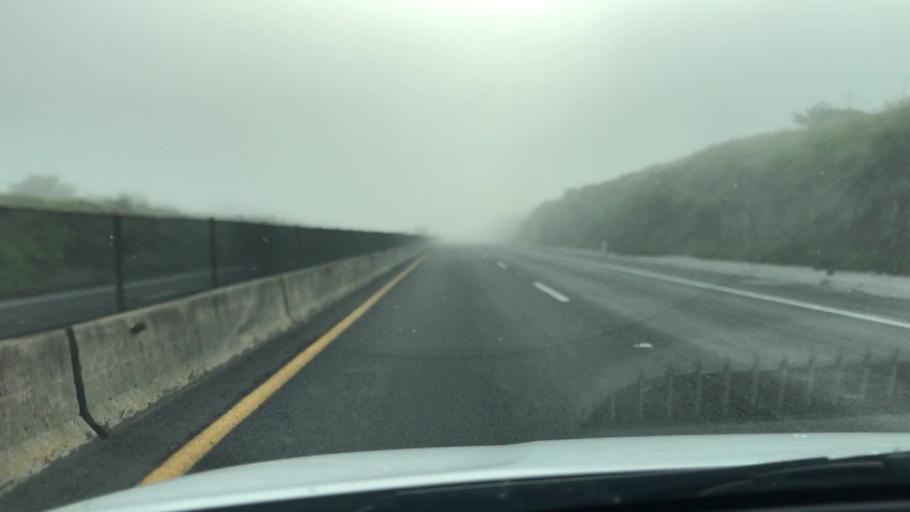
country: MX
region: Jalisco
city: Jalostotitlan
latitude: 21.0708
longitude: -102.5072
